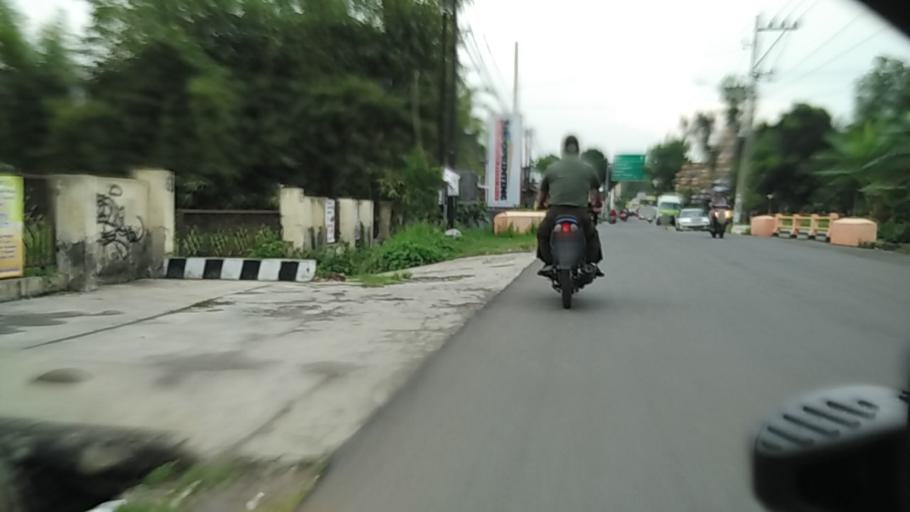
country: ID
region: Central Java
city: Semarang
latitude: -7.0648
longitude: 110.4279
